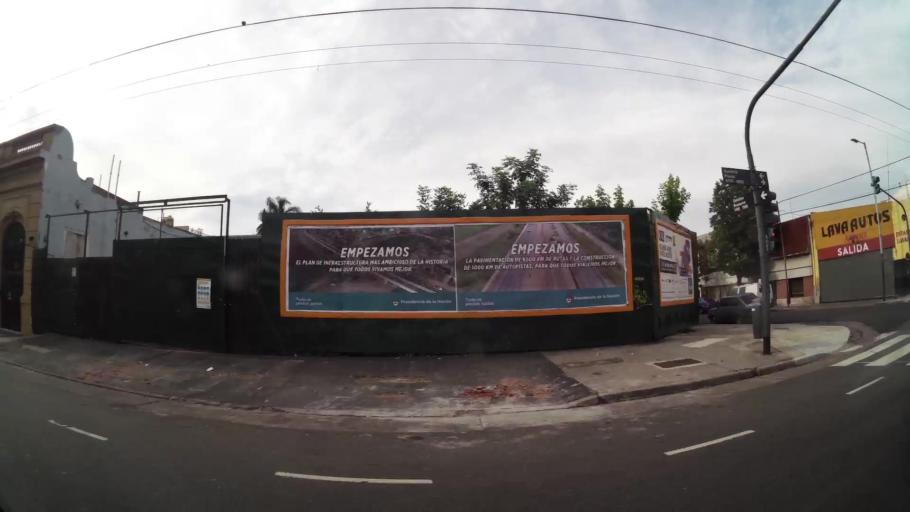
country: AR
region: Buenos Aires F.D.
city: Buenos Aires
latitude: -34.6307
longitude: -58.4207
